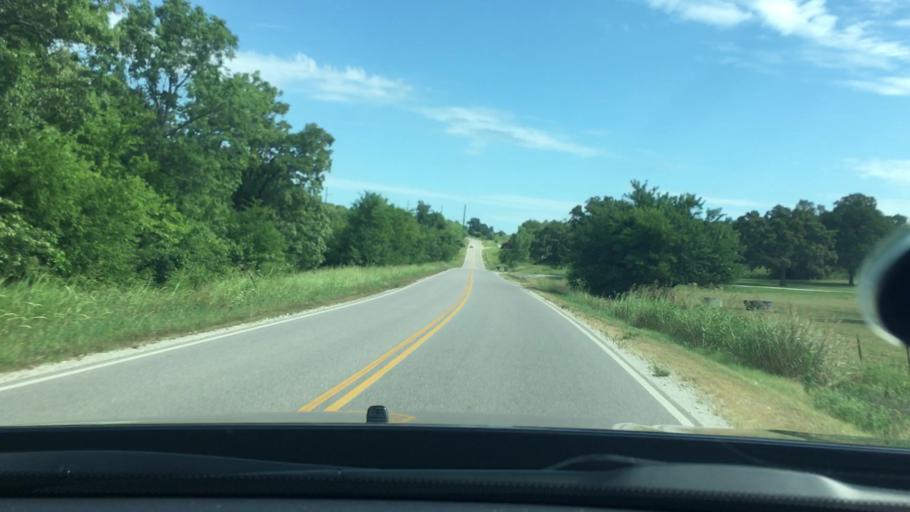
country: US
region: Oklahoma
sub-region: Pontotoc County
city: Ada
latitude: 34.7672
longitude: -96.5820
